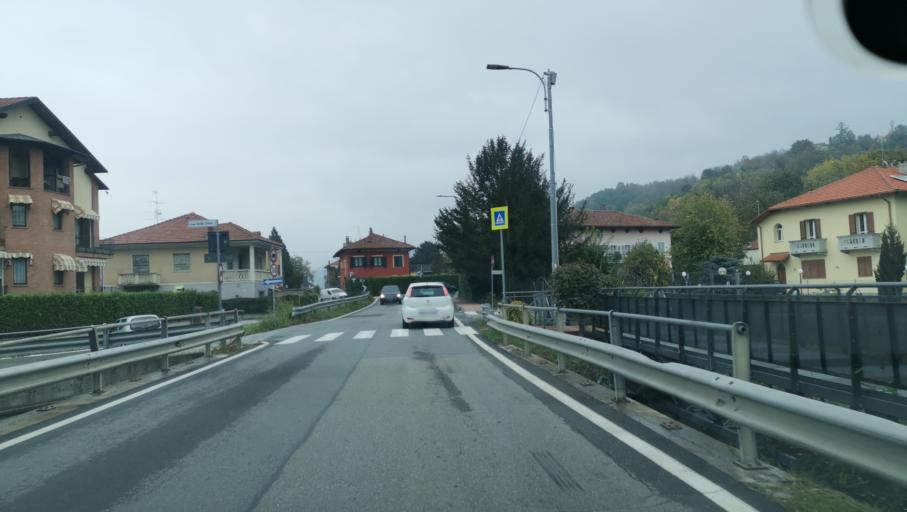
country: IT
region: Piedmont
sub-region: Provincia di Torino
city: Gassino Torinese
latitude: 45.1305
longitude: 7.8307
